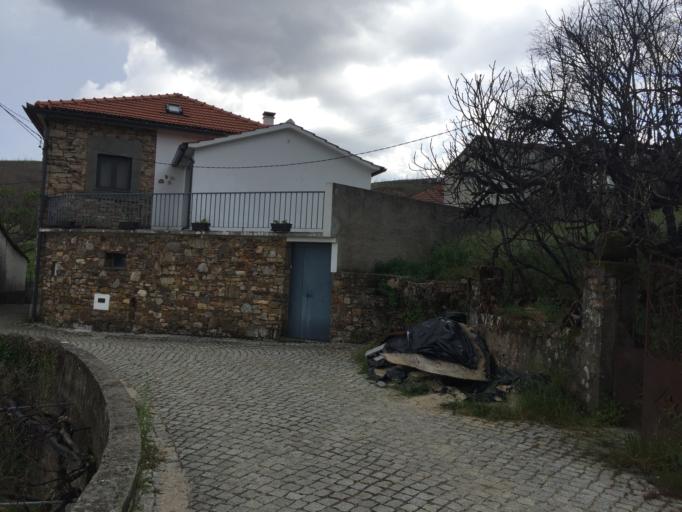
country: PT
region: Coimbra
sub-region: Pampilhosa da Serra
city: Pampilhosa da Serra
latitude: 40.1496
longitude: -7.9243
